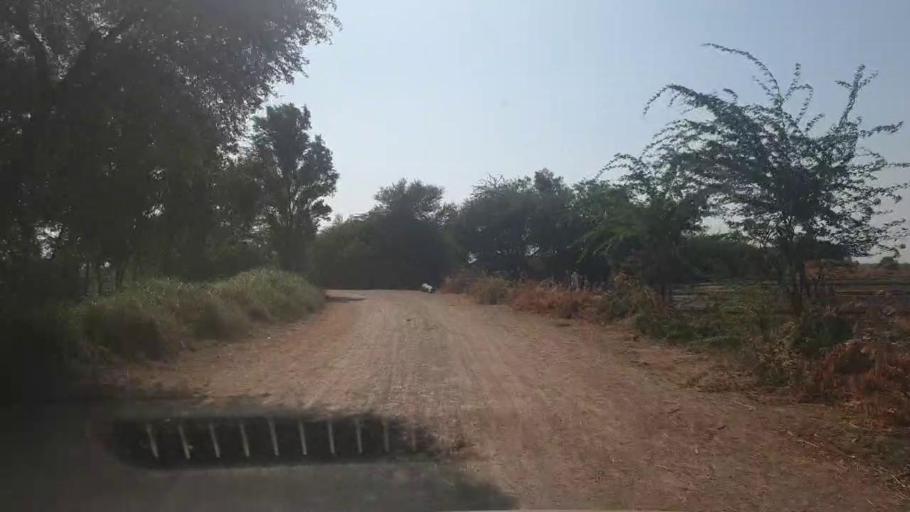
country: PK
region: Sindh
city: Badin
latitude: 24.5498
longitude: 68.8455
